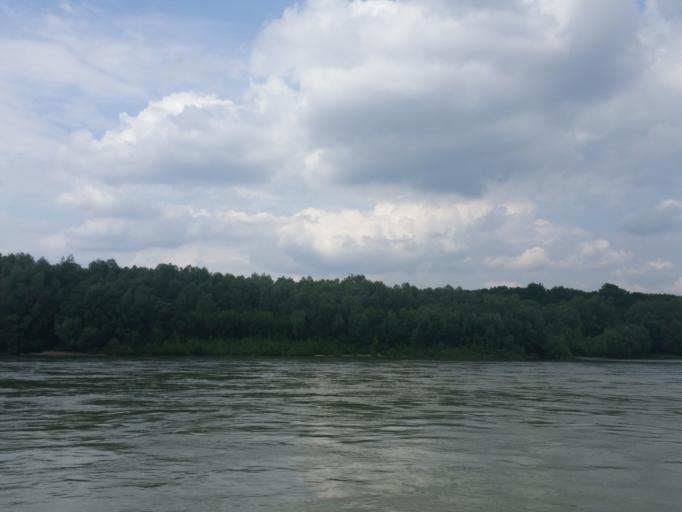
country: AT
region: Lower Austria
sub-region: Politischer Bezirk Bruck an der Leitha
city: Petronell-Carnuntum
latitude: 48.1284
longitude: 16.8713
